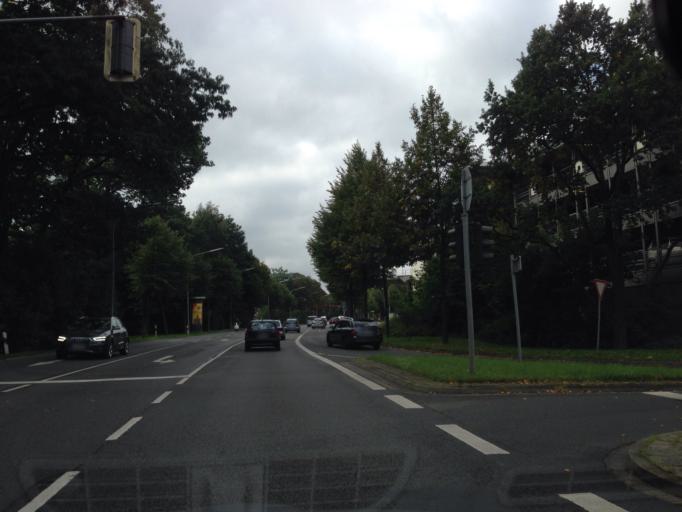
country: DE
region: Lower Saxony
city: Lueneburg
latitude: 53.2549
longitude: 10.4177
